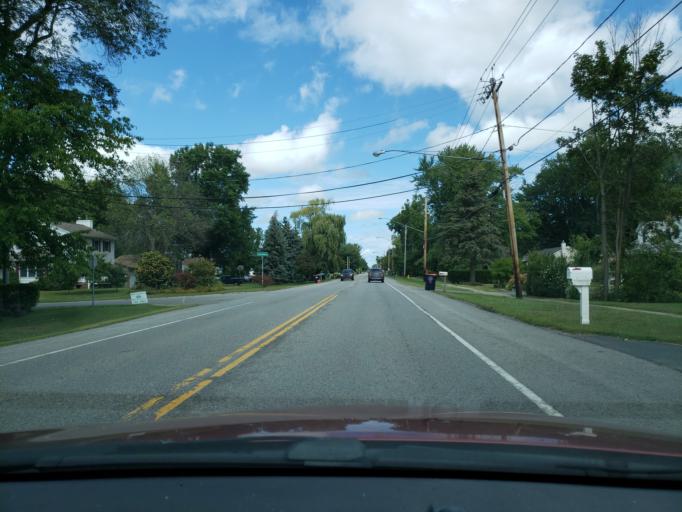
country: US
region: New York
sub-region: Monroe County
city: Greece
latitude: 43.2220
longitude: -77.7338
